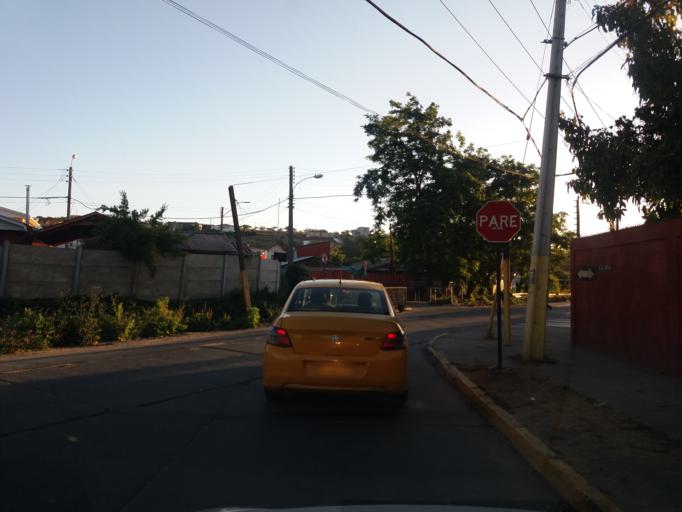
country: CL
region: Valparaiso
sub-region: Provincia de Quillota
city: Quillota
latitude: -32.9383
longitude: -71.2745
